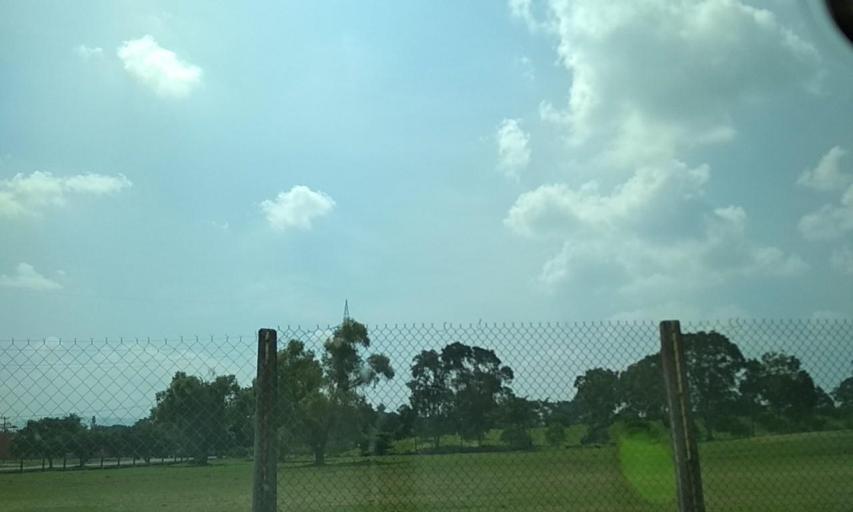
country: MX
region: Veracruz
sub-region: Tlapacoyan
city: San Pedro Tlapacoyan
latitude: 20.0637
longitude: -97.0825
